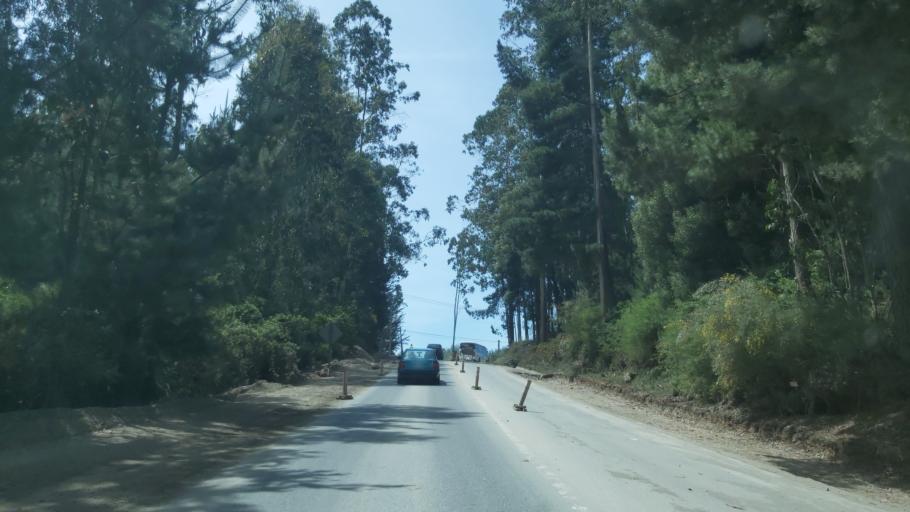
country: CL
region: Maule
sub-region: Provincia de Talca
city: Constitucion
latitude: -35.3770
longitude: -72.4218
